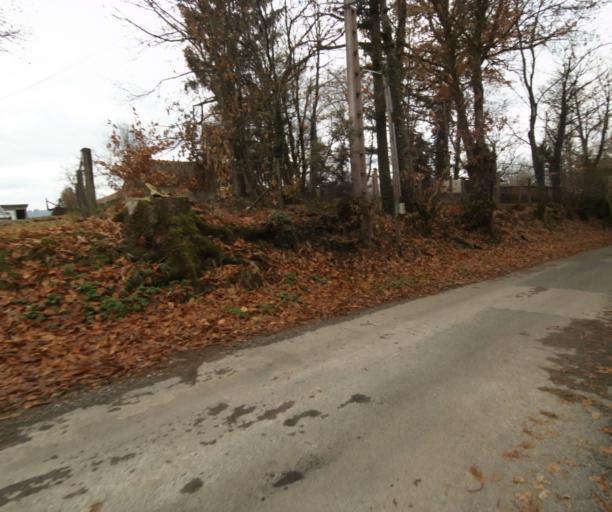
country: FR
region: Limousin
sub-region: Departement de la Correze
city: Laguenne
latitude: 45.2344
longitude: 1.7477
